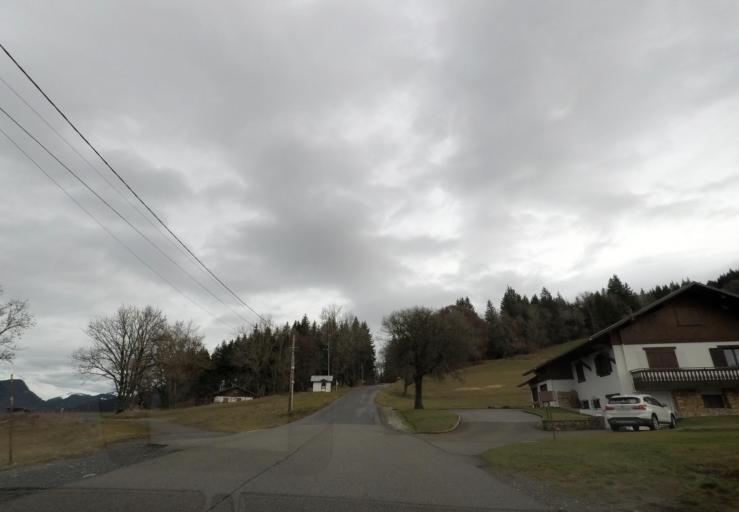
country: FR
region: Rhone-Alpes
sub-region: Departement de la Haute-Savoie
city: Chatillon-sur-Cluses
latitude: 46.0807
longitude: 6.6108
